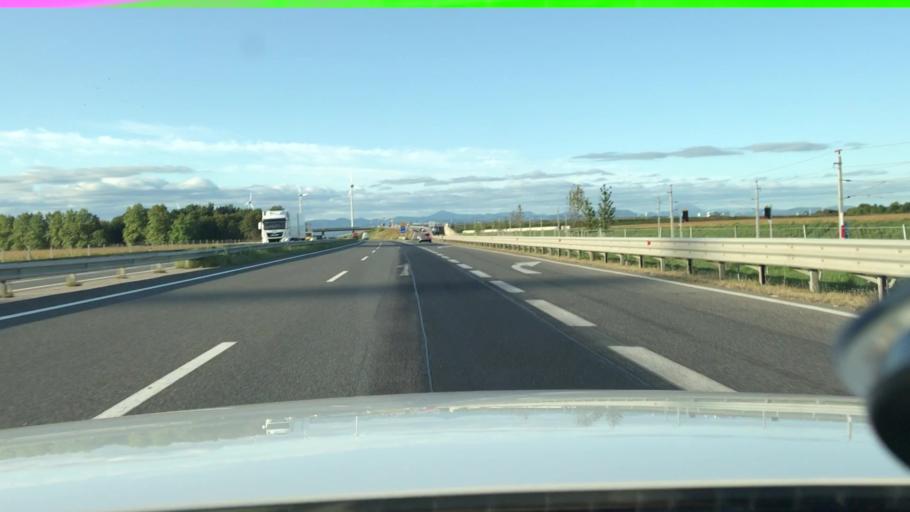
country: AT
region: Lower Austria
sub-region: Sankt Polten Stadt
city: Sankt Poelten
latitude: 48.2039
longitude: 15.6639
